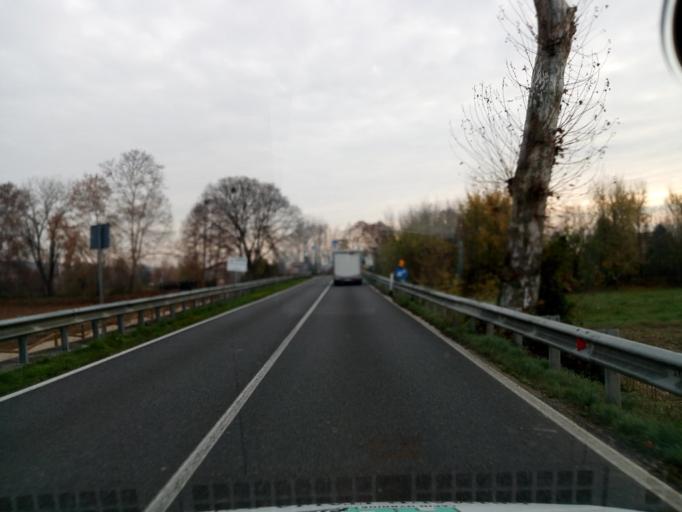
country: IT
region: Veneto
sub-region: Provincia di Treviso
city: Villa d'Asolo
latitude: 45.7858
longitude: 11.8934
